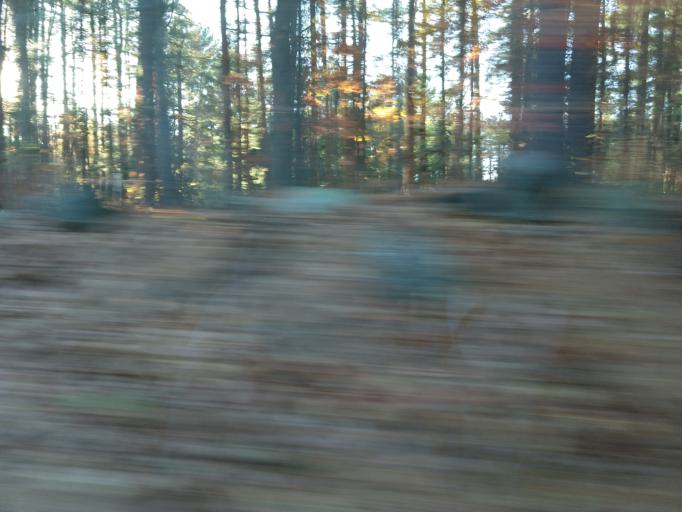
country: US
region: Massachusetts
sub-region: Middlesex County
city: West Concord
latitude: 42.4349
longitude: -71.3724
